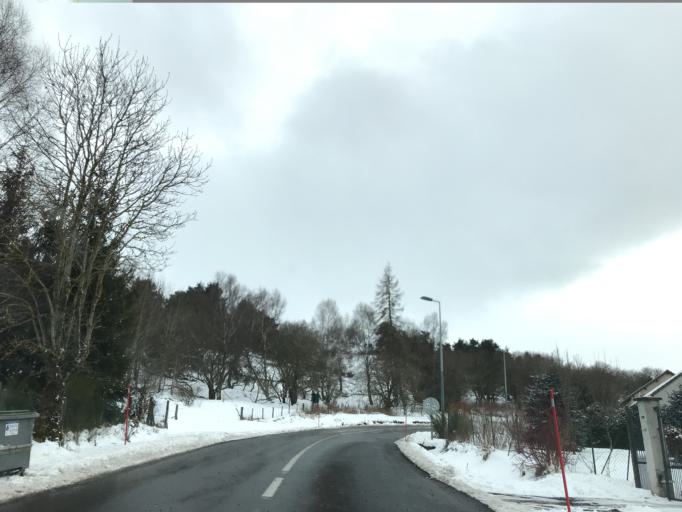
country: FR
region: Auvergne
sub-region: Departement du Puy-de-Dome
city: Aydat
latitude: 45.6847
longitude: 2.9387
